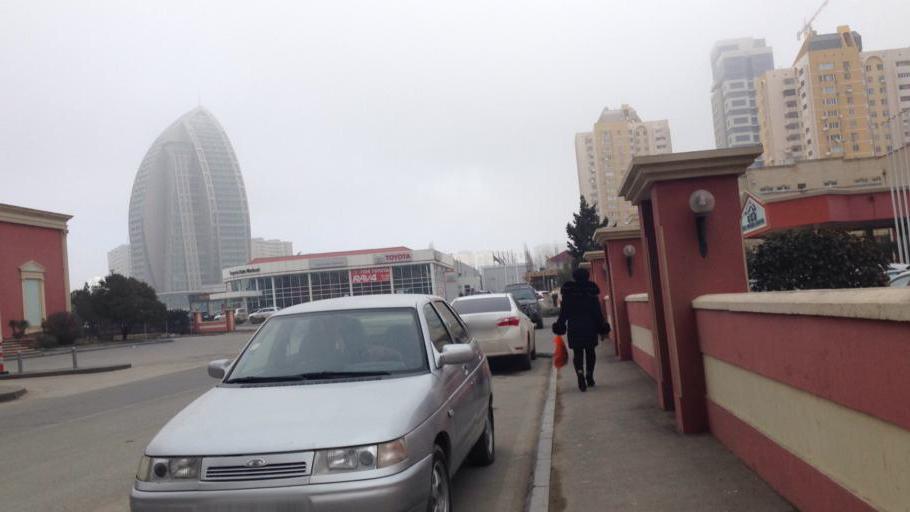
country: AZ
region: Baki
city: Baku
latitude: 40.3842
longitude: 49.8682
